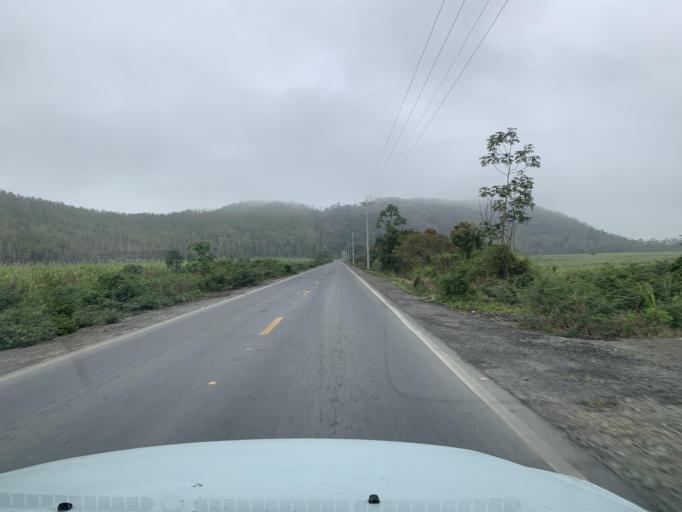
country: EC
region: Guayas
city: Coronel Marcelino Mariduena
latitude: -2.3485
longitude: -79.5294
